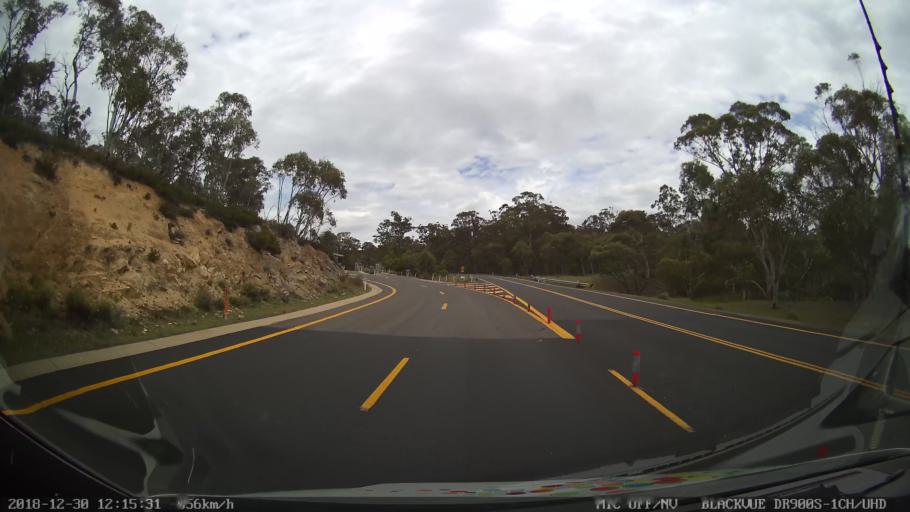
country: AU
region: New South Wales
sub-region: Snowy River
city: Jindabyne
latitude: -36.3451
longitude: 148.5705
